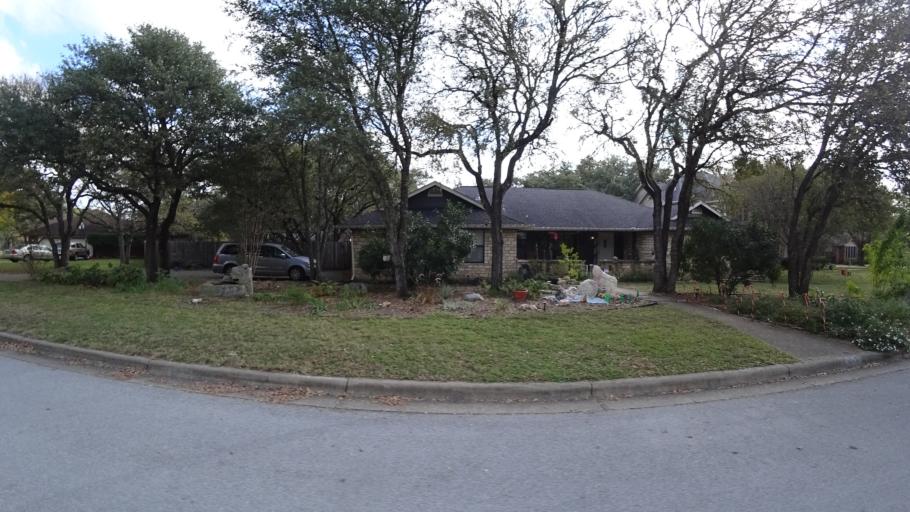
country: US
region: Texas
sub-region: Travis County
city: Shady Hollow
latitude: 30.1718
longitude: -97.8607
